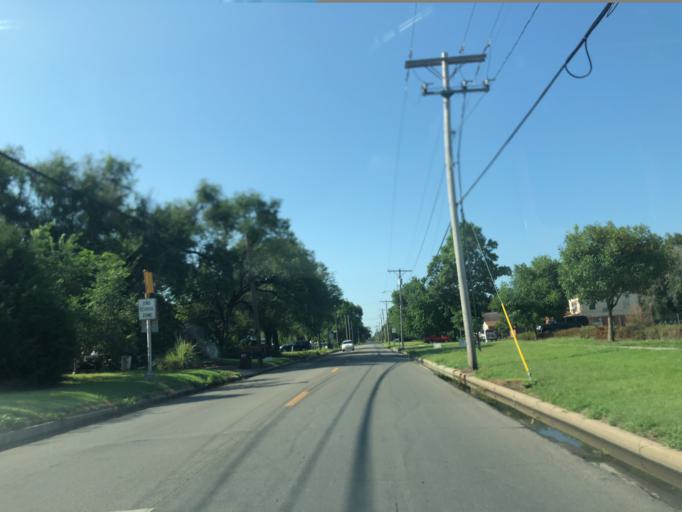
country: US
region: Kansas
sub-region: Sedgwick County
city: Wichita
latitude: 37.7449
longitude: -97.3448
